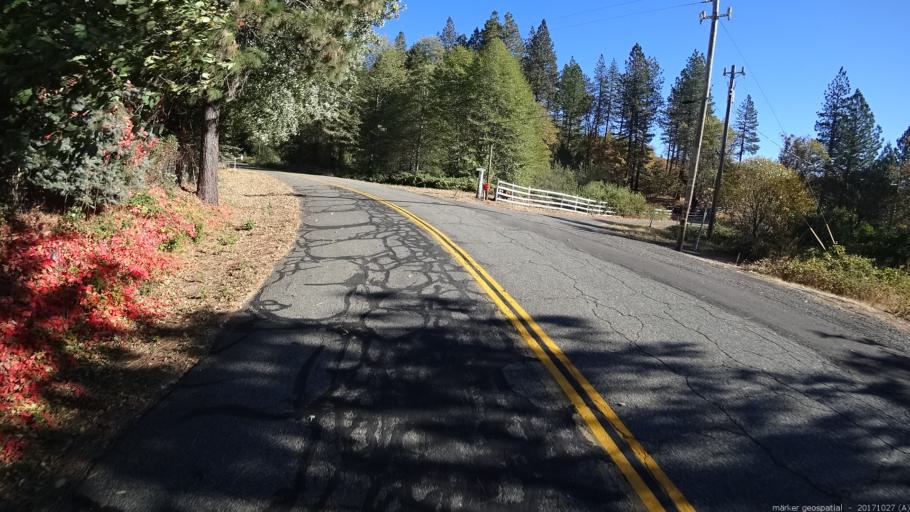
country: US
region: California
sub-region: Shasta County
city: Burney
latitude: 40.8480
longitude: -121.9089
